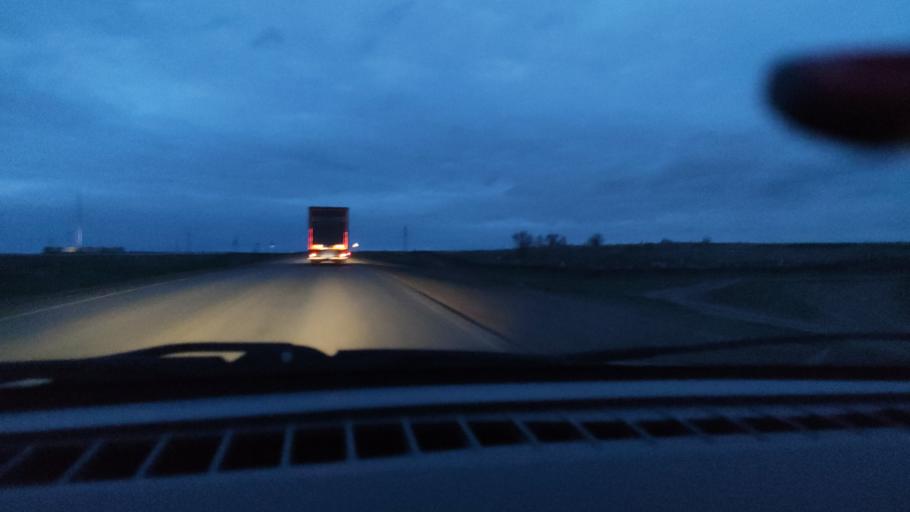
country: RU
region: Orenburg
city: Tatarskaya Kargala
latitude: 51.9519
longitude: 55.1830
